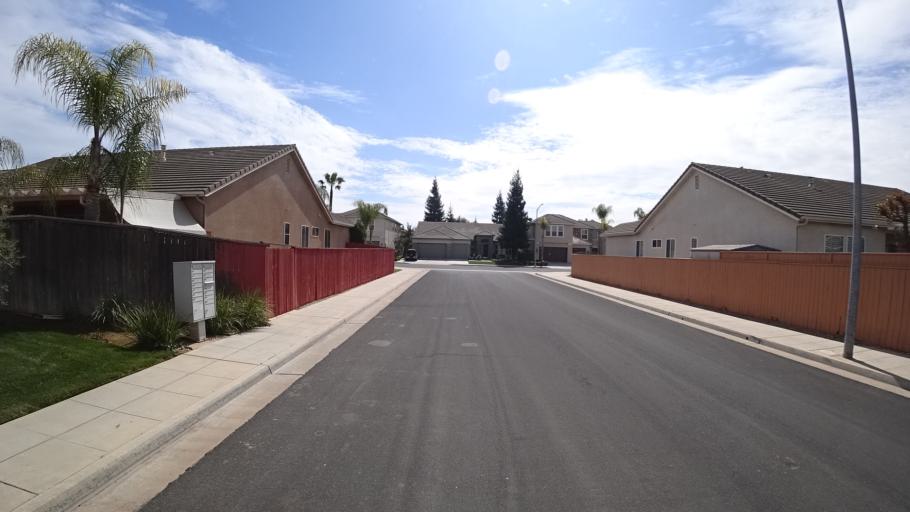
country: US
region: California
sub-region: Fresno County
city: Biola
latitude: 36.8423
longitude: -119.8950
